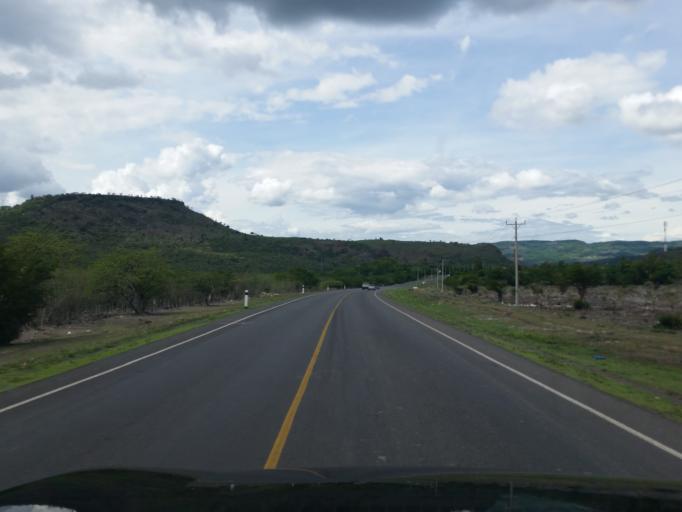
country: NI
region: Boaco
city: Teustepe
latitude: 12.4360
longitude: -86.0424
